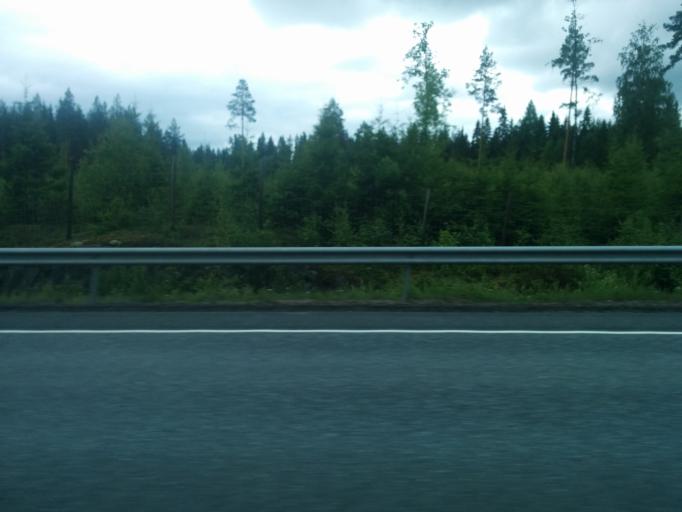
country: FI
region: Pirkanmaa
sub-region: Tampere
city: Orivesi
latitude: 61.6789
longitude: 24.3233
